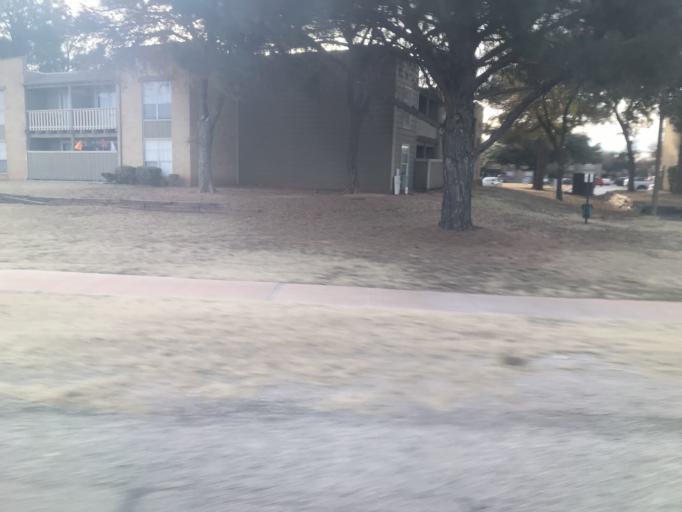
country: US
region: Texas
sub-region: Taylor County
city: Abilene
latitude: 32.4221
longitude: -99.7839
